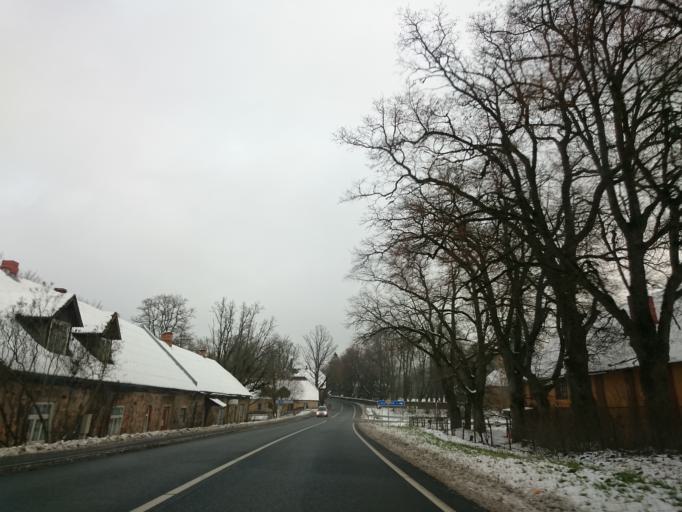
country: LV
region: Pargaujas
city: Stalbe
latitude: 57.3470
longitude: 24.9442
